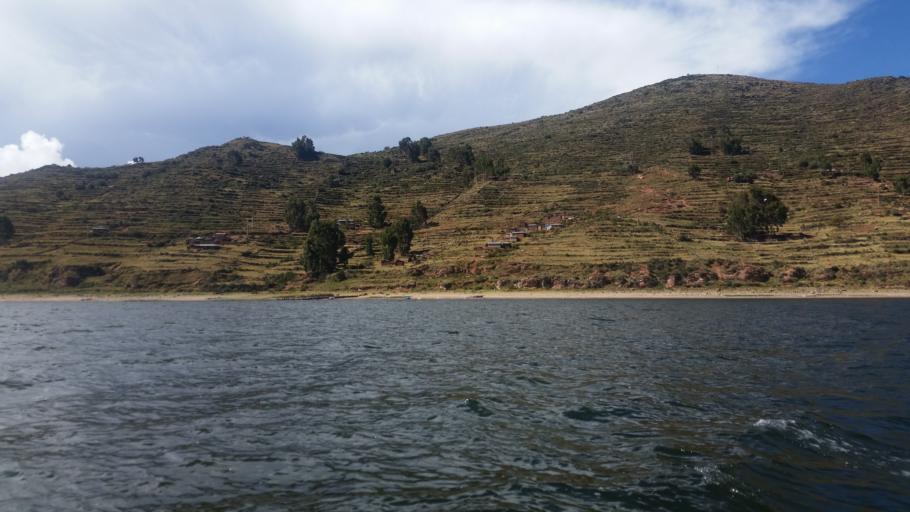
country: PE
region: Puno
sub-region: Provincia de Puno
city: Taquile
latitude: -15.7309
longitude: -69.7619
